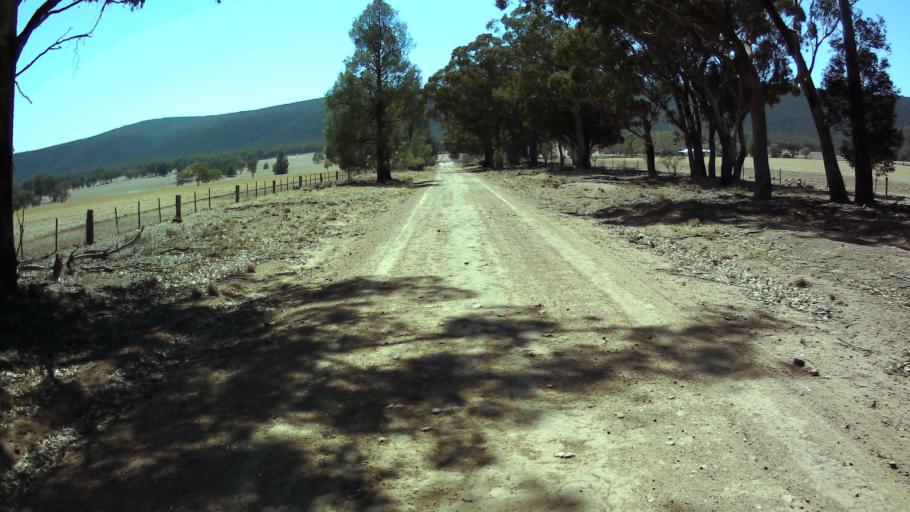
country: AU
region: New South Wales
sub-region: Weddin
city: Grenfell
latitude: -33.7032
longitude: 148.3334
